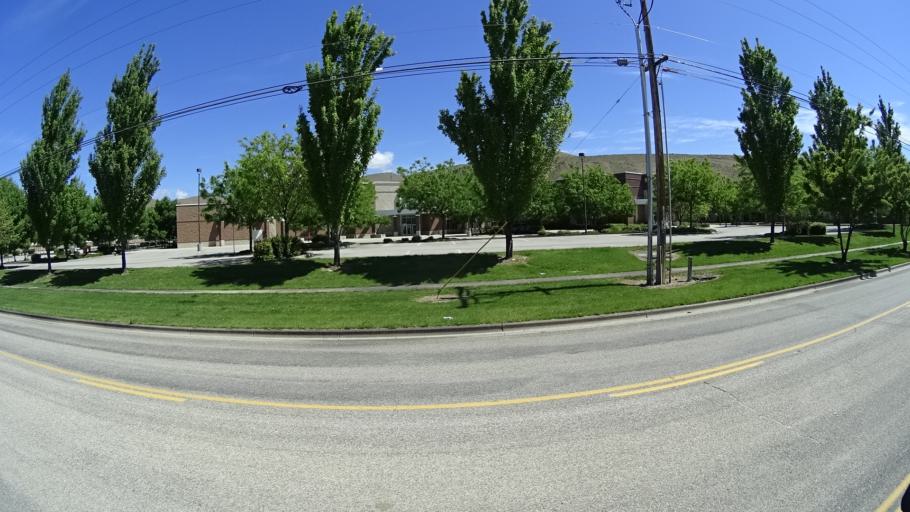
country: US
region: Idaho
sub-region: Ada County
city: Boise
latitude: 43.5653
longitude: -116.1141
